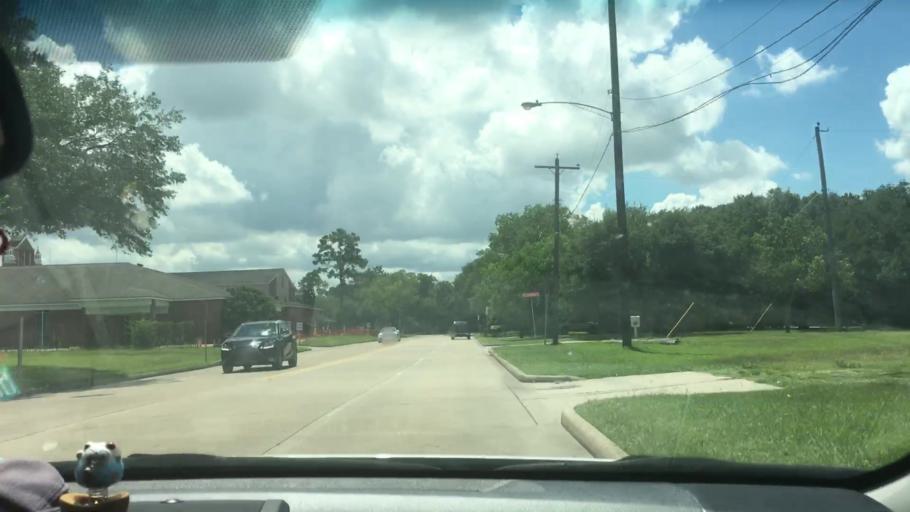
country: US
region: Texas
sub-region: Fort Bend County
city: Missouri City
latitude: 29.6144
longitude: -95.5465
